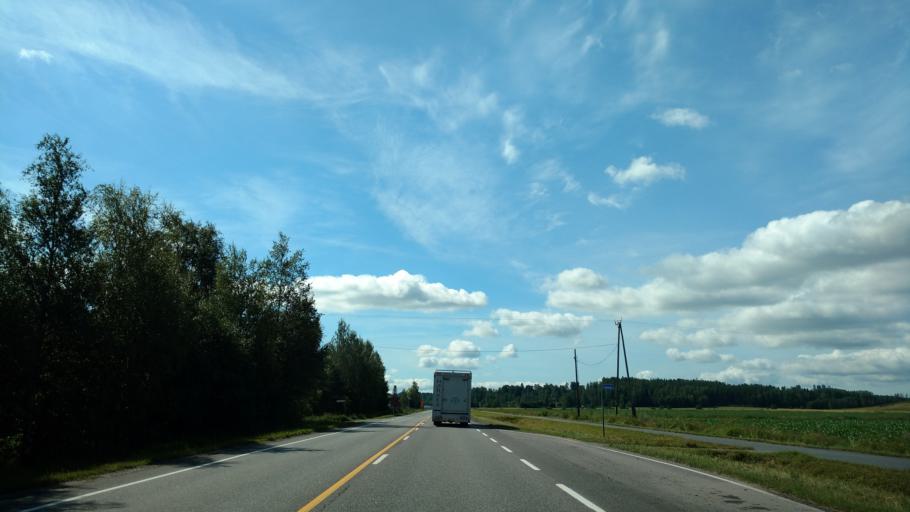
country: FI
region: Varsinais-Suomi
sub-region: Salo
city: Pernioe
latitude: 60.2306
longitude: 23.1233
